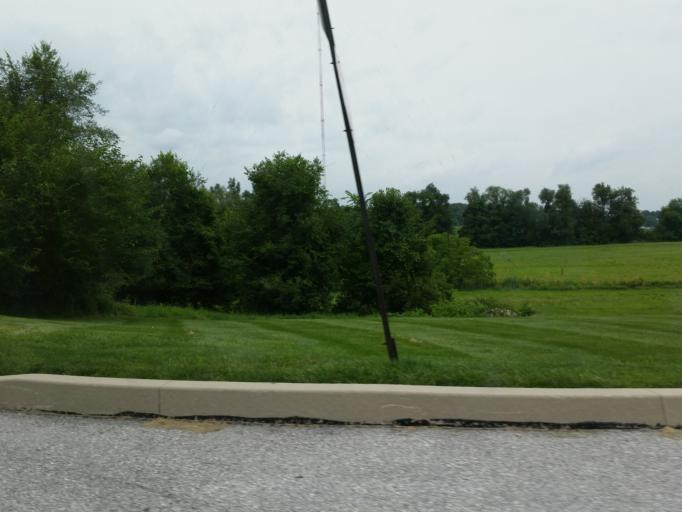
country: US
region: Pennsylvania
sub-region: York County
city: North York
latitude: 39.9988
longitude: -76.7470
